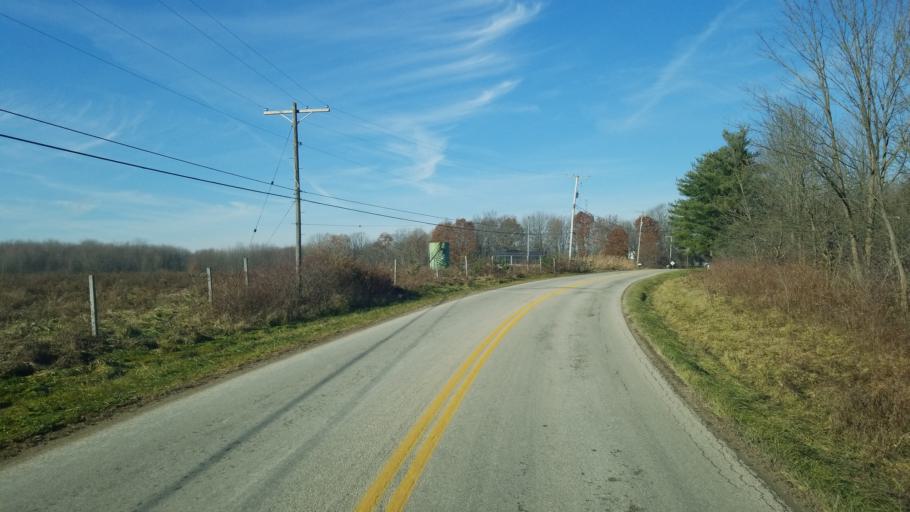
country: US
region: Ohio
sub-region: Ashtabula County
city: Jefferson
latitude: 41.7177
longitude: -80.6931
